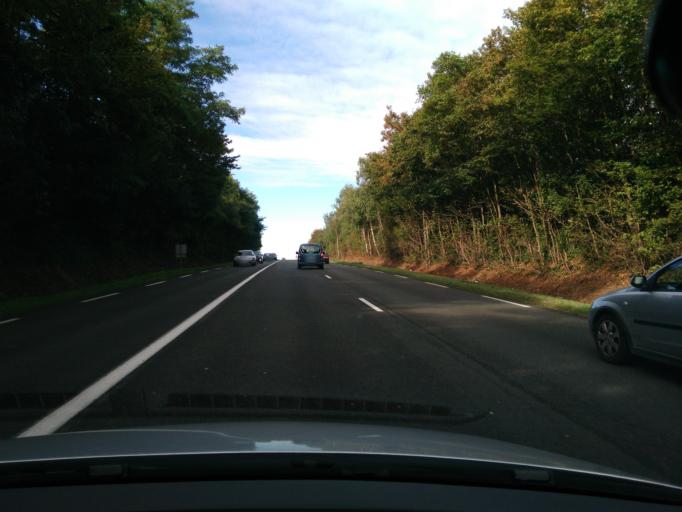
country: FR
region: Centre
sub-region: Departement d'Eure-et-Loir
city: Dreux
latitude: 48.7458
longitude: 1.3749
